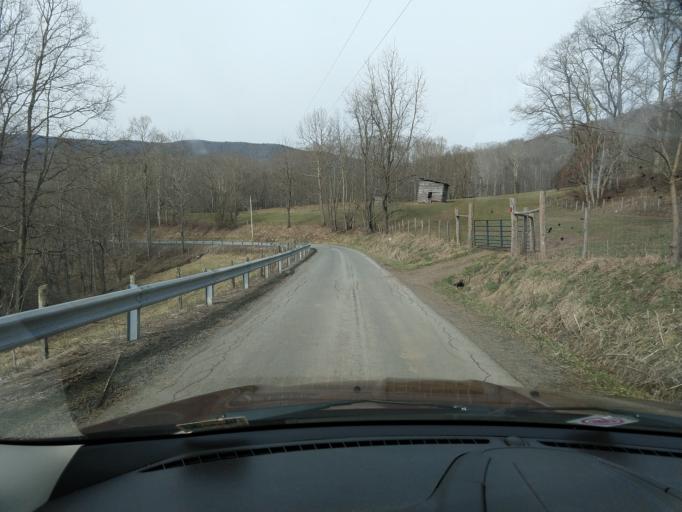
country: US
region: West Virginia
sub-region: Tucker County
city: Parsons
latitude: 39.0256
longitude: -79.5621
